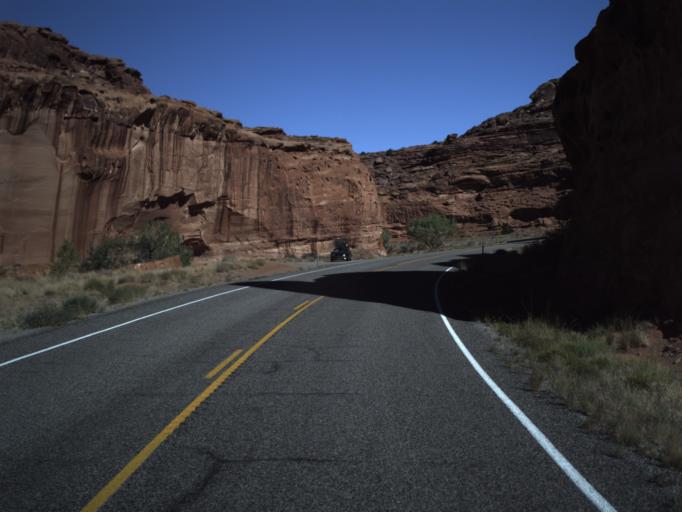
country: US
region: Utah
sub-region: San Juan County
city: Blanding
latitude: 37.9848
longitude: -110.4931
